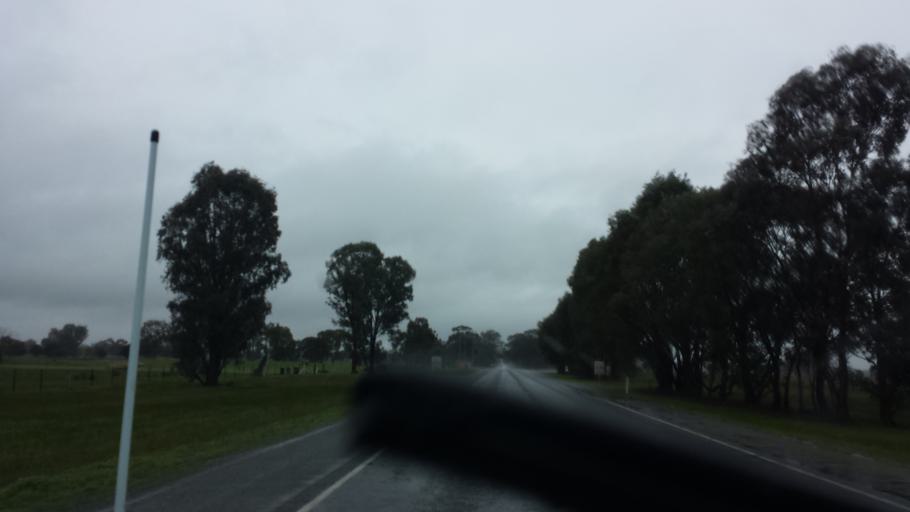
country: AU
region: Victoria
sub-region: Benalla
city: Benalla
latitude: -36.5412
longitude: 146.0148
